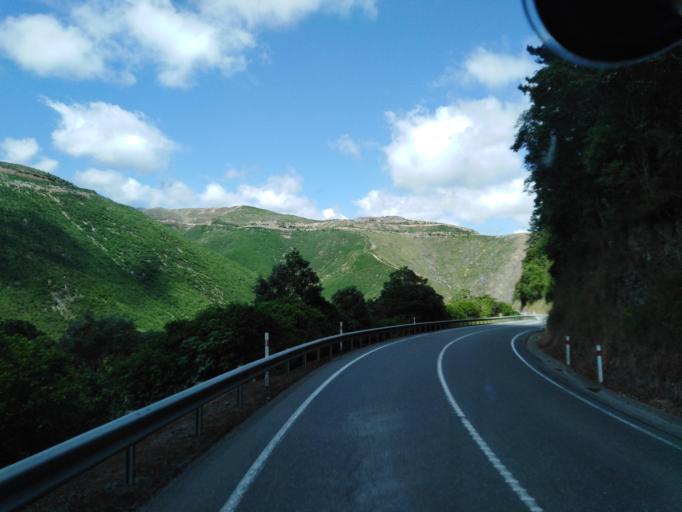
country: NZ
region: Nelson
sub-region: Nelson City
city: Nelson
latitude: -41.2276
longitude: 173.4172
